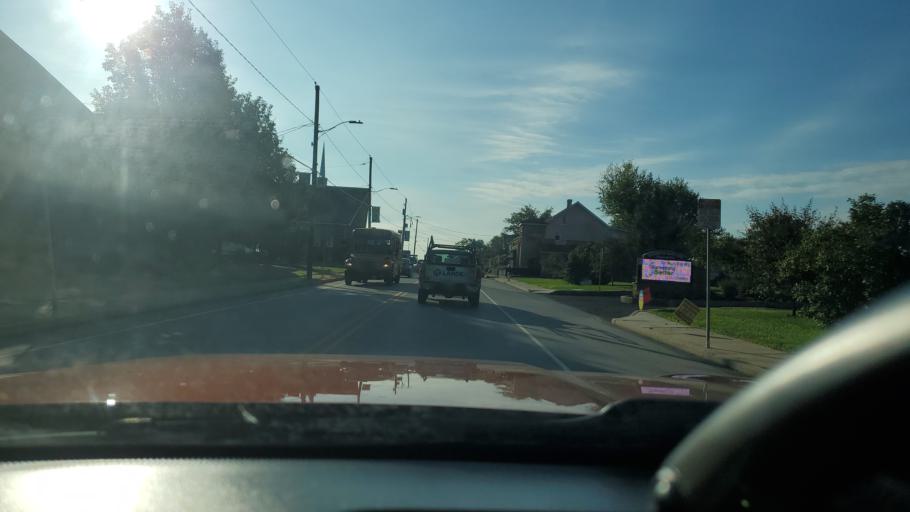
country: US
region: Pennsylvania
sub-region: Montgomery County
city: Souderton
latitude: 40.3149
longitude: -75.3301
